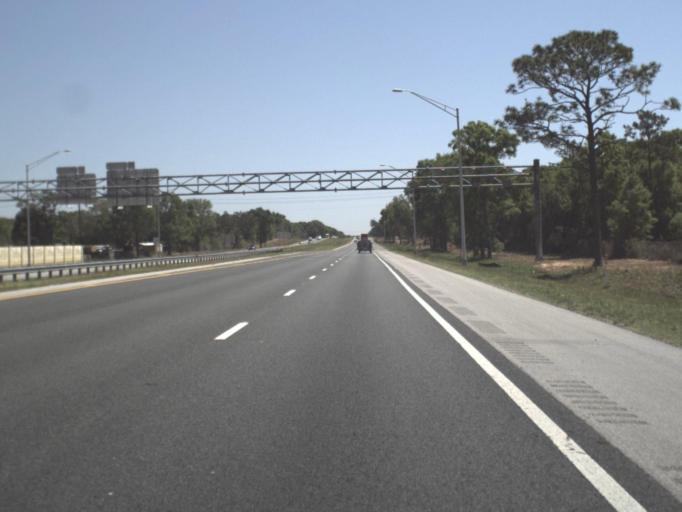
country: US
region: Florida
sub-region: Escambia County
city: Ferry Pass
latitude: 30.5028
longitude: -87.2090
